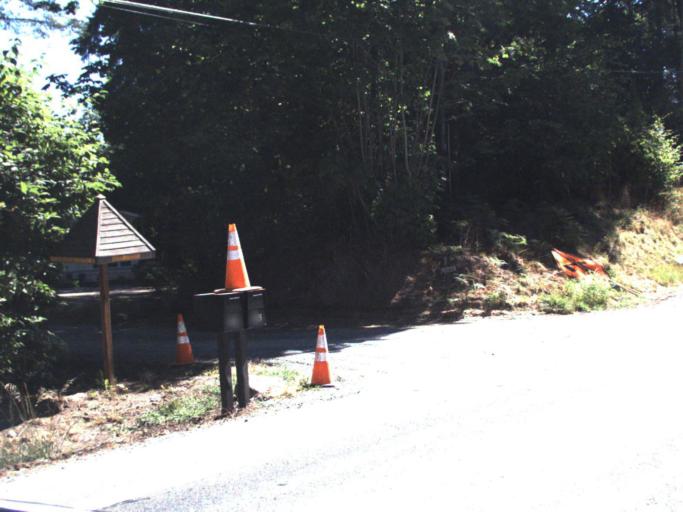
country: US
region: Washington
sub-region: King County
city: East Renton Highlands
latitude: 47.5019
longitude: -122.1276
